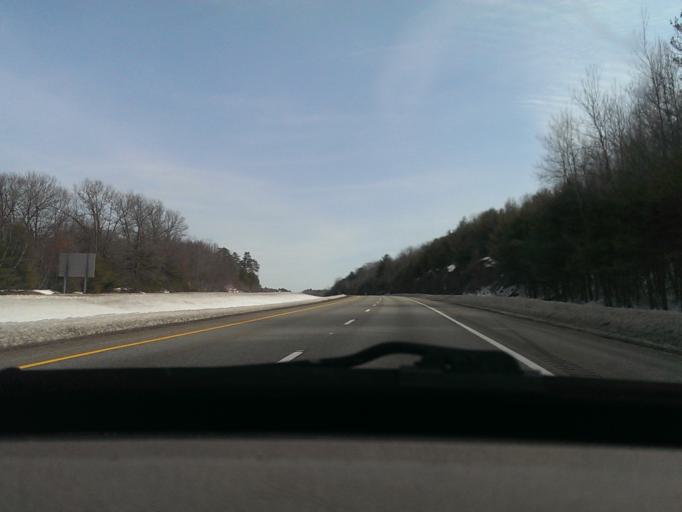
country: US
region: Massachusetts
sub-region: Worcester County
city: Millville
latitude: 42.0312
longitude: -71.6177
